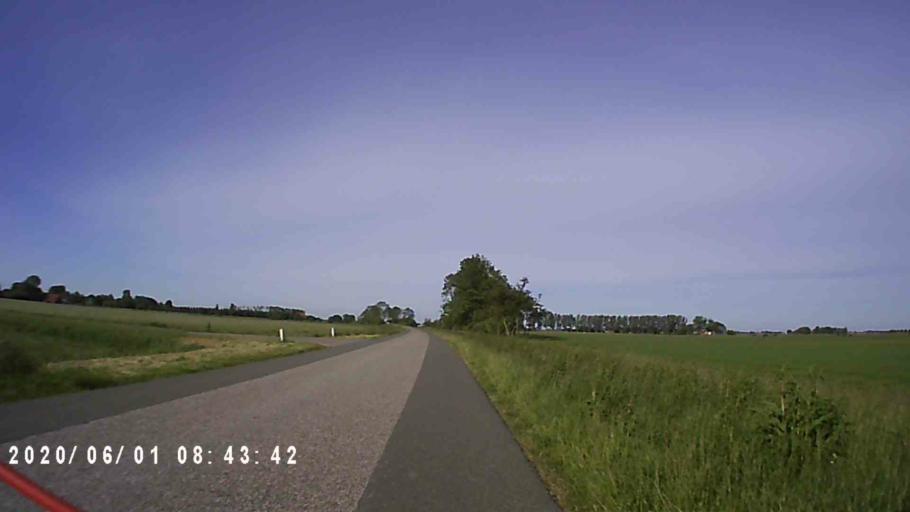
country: NL
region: Friesland
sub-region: Gemeente Ferwerderadiel
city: Burdaard
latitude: 53.2825
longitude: 5.8411
